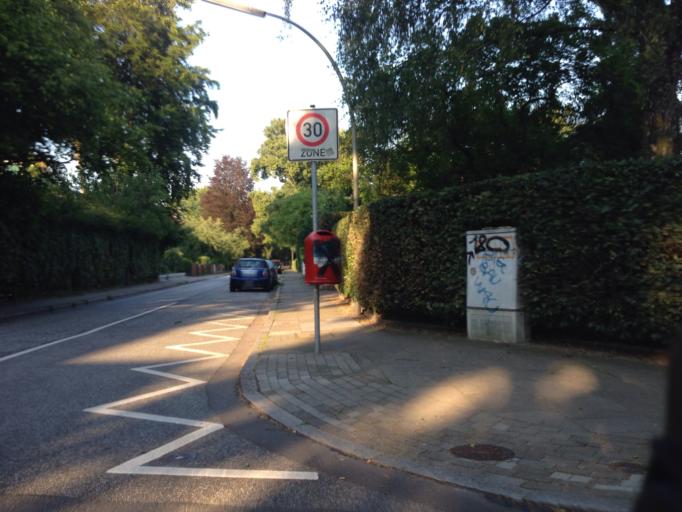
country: DE
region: Hamburg
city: Marienthal
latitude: 53.5688
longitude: 10.0683
